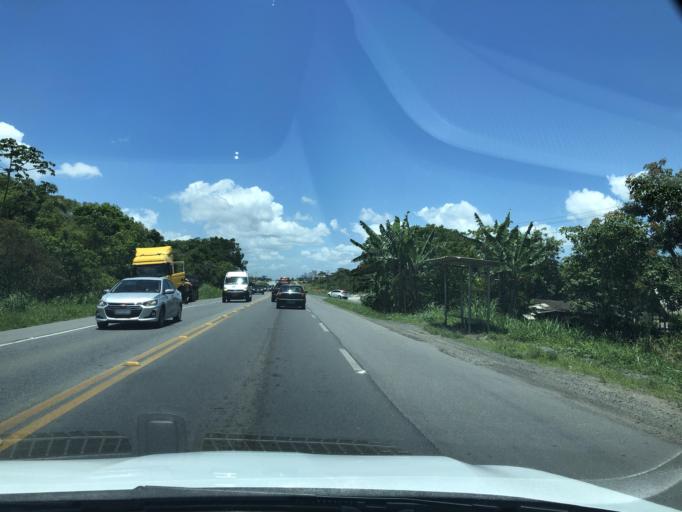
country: BR
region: Santa Catarina
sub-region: Joinville
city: Joinville
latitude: -26.3818
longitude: -48.7248
